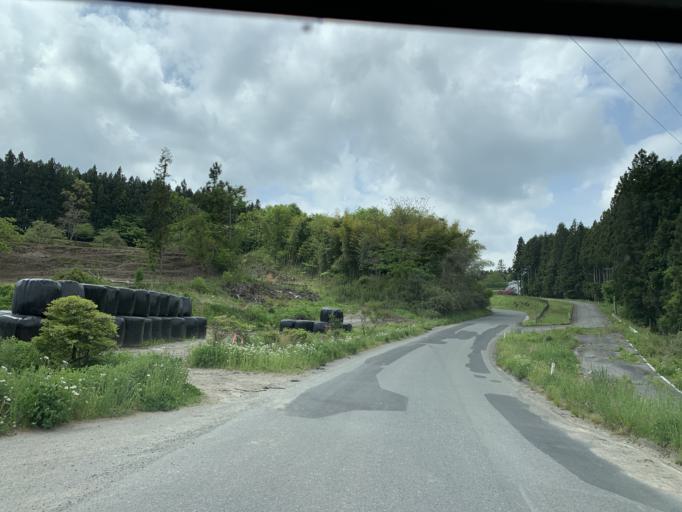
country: JP
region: Miyagi
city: Furukawa
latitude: 38.7307
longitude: 140.9276
